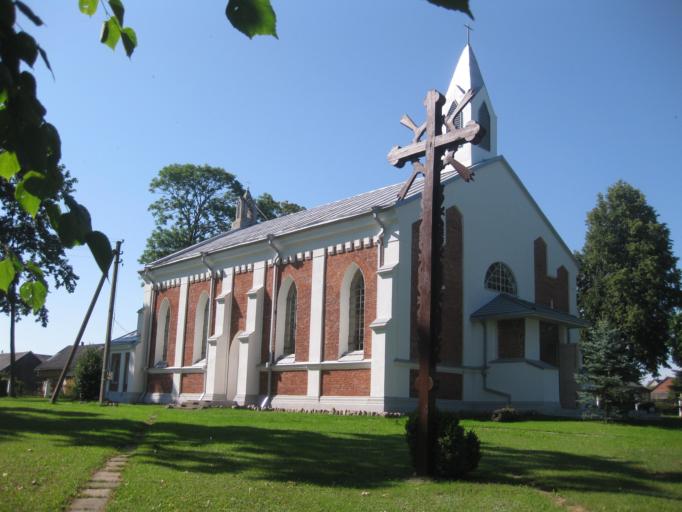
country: LT
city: Birstonas
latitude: 54.7233
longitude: 24.0543
